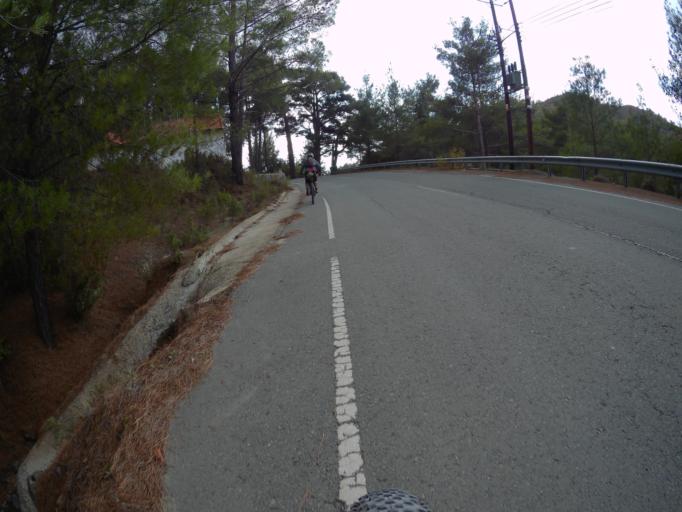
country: CY
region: Lefkosia
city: Kakopetria
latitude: 34.9183
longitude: 32.8141
